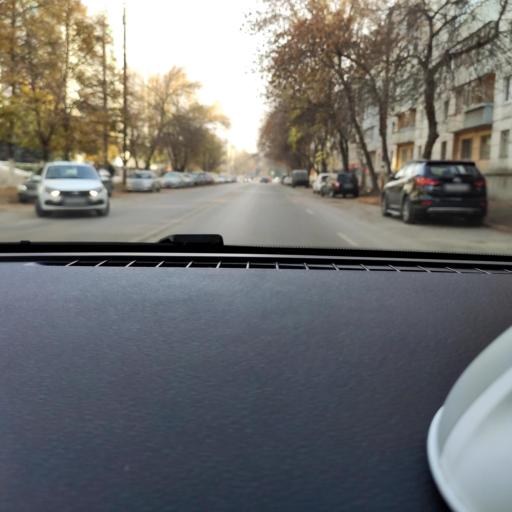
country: RU
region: Samara
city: Samara
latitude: 53.2082
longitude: 50.2291
